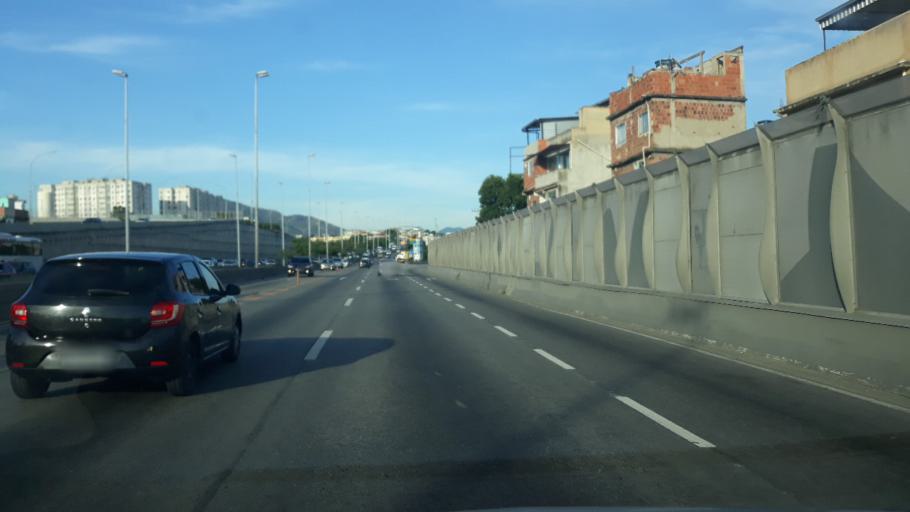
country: BR
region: Rio de Janeiro
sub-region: Rio De Janeiro
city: Rio de Janeiro
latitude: -22.8815
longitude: -43.2829
